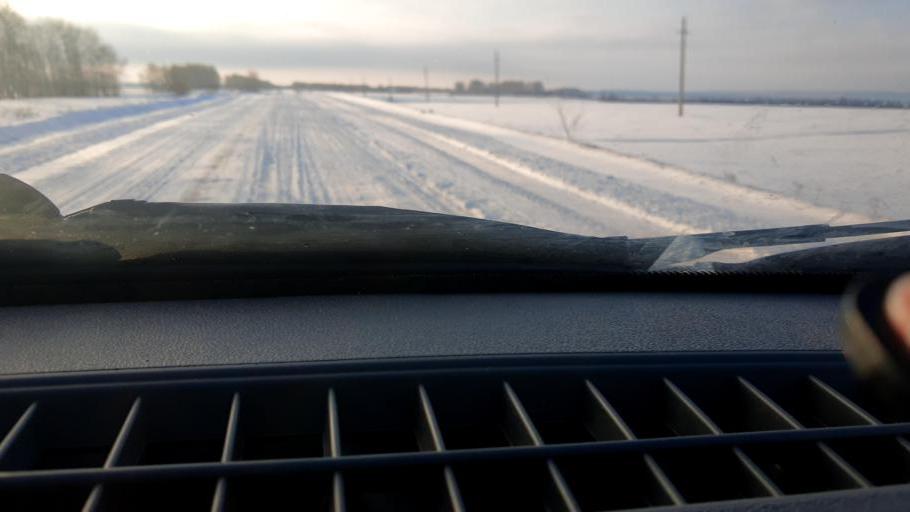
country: RU
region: Bashkortostan
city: Kushnarenkovo
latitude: 55.1195
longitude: 55.5781
